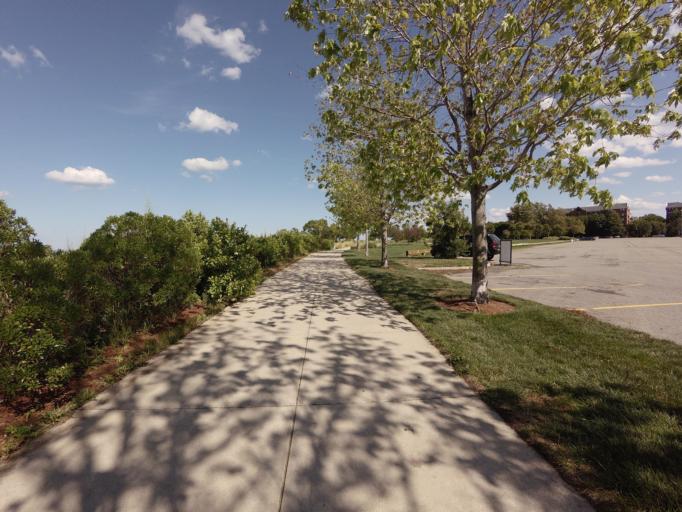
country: US
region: Massachusetts
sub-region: Suffolk County
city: South Boston
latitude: 42.3230
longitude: -71.0452
